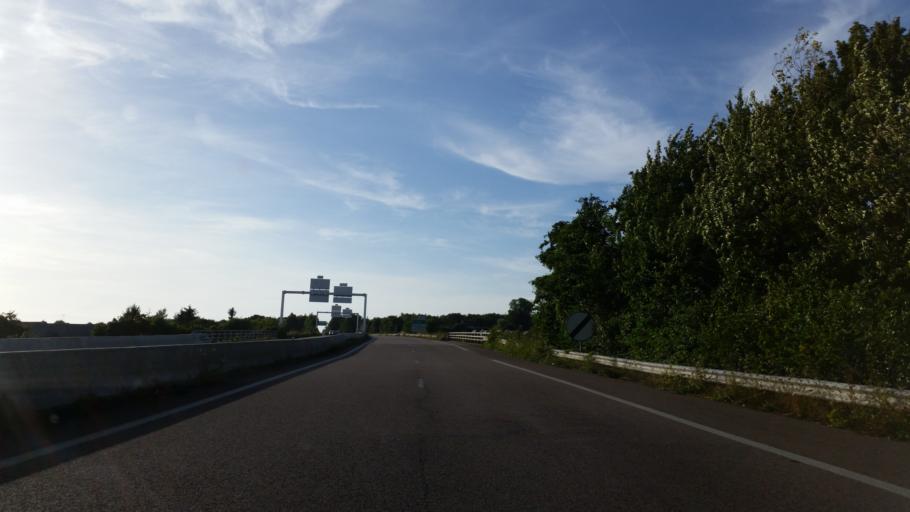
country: FR
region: Lower Normandy
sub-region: Departement du Calvados
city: Saint-Gatien-des-Bois
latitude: 49.2940
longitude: 0.1984
